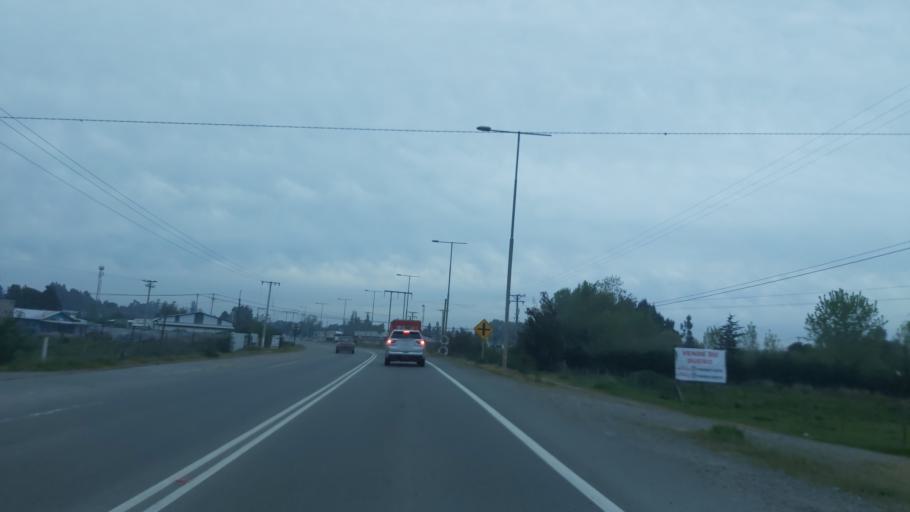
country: CL
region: Maule
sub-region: Provincia de Linares
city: Linares
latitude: -35.8370
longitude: -71.6228
